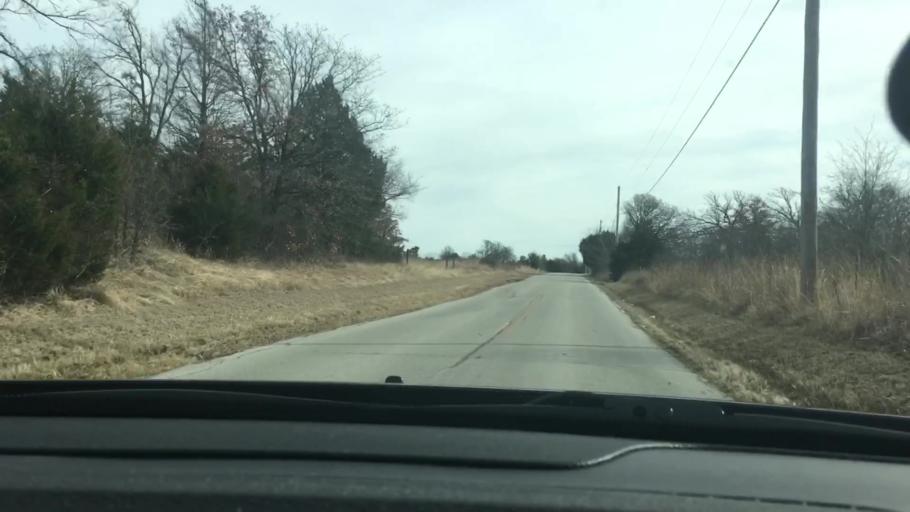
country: US
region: Oklahoma
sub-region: Carter County
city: Ardmore
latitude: 34.1742
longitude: -97.0827
